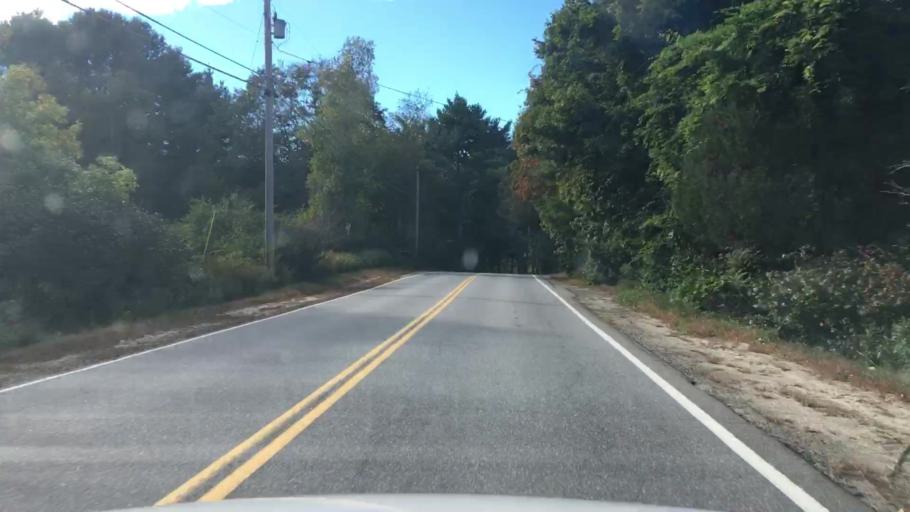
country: US
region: Maine
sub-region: Sagadahoc County
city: Topsham
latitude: 43.9318
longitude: -70.0083
